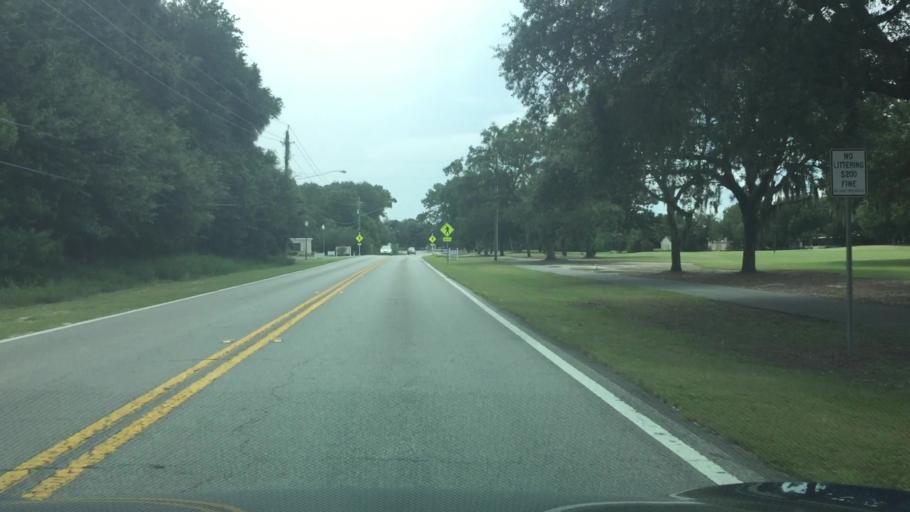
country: US
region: Florida
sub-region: Bay County
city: Upper Grand Lagoon
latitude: 30.1531
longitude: -85.7267
